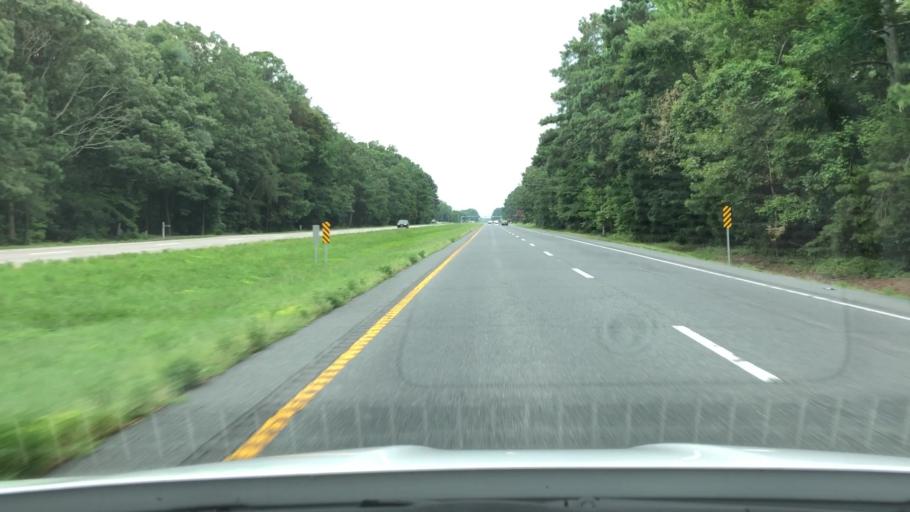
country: US
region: Virginia
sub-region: Northampton County
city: Eastville
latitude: 37.3580
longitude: -75.9349
